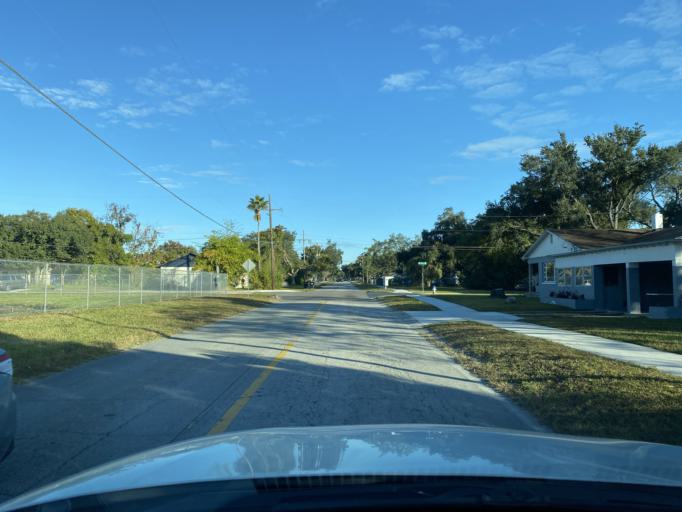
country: US
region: Florida
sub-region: Orange County
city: Orlando
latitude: 28.5224
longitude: -81.3888
